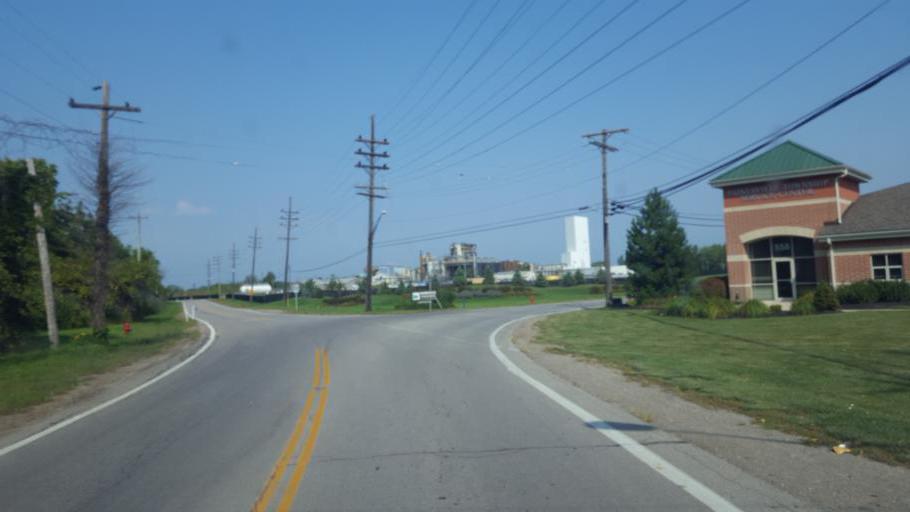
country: US
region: Ohio
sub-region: Lake County
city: Painesville
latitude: 41.7534
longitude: -81.2303
